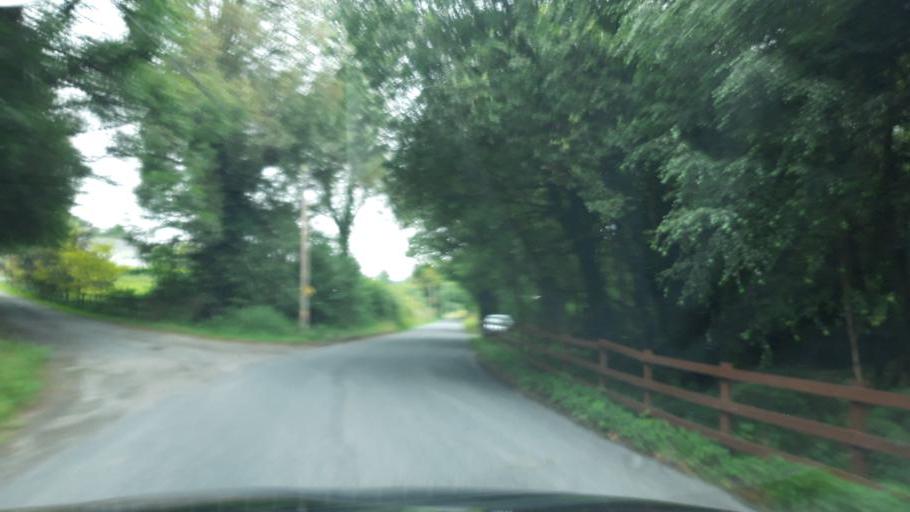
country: IE
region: Leinster
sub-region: Kilkenny
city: Ballyragget
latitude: 52.7230
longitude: -7.4006
